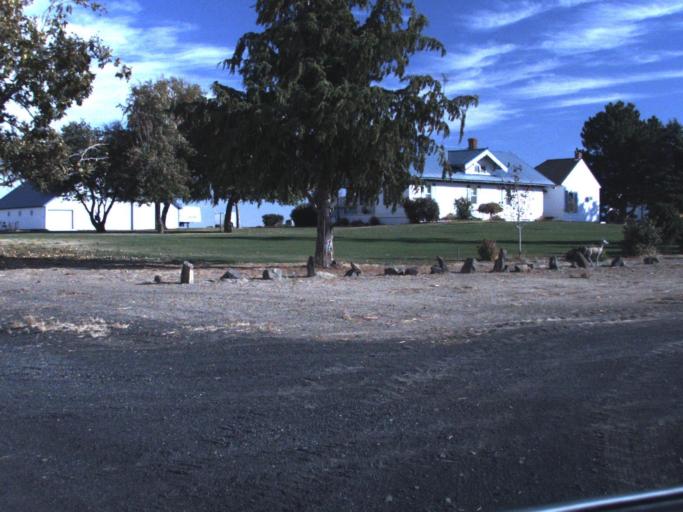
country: US
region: Washington
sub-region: Adams County
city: Ritzville
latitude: 47.2808
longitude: -118.6907
